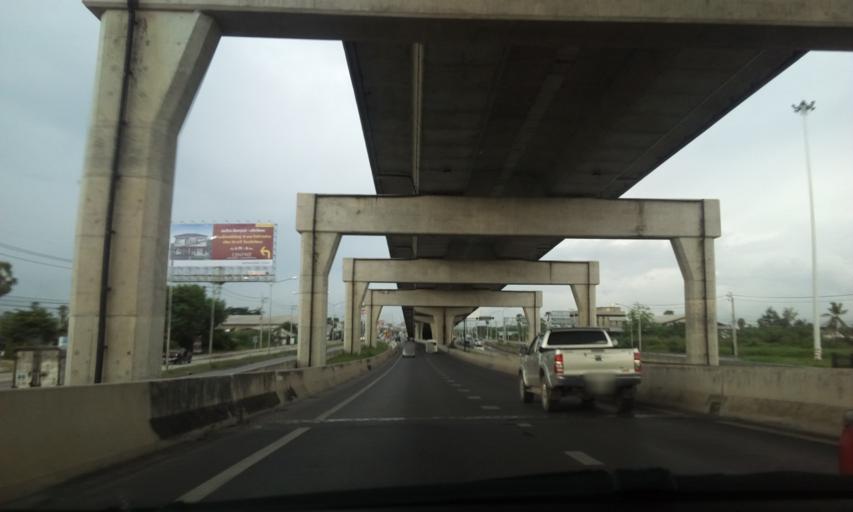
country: TH
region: Nonthaburi
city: Bang Bua Thong
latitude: 13.9276
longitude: 100.4552
